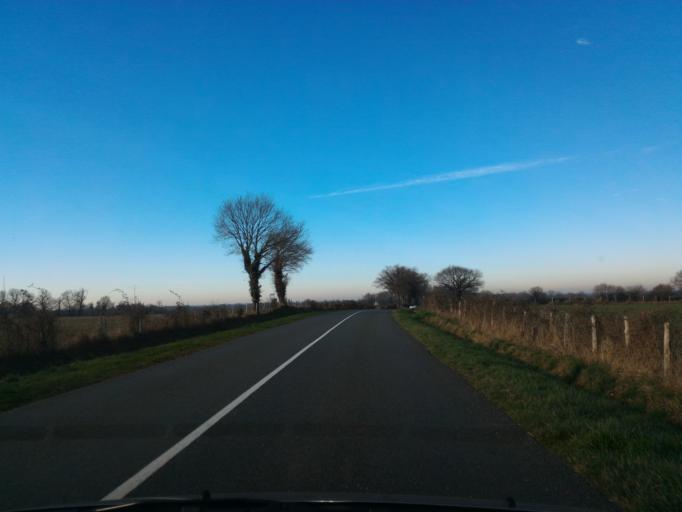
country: FR
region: Poitou-Charentes
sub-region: Departement de la Charente
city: Confolens
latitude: 46.0306
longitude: 0.5674
